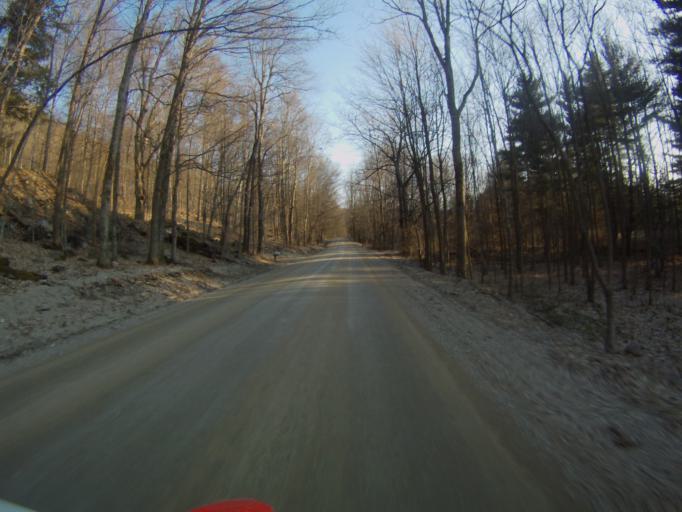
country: US
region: Vermont
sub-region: Addison County
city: Bristol
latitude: 44.1029
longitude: -73.0748
